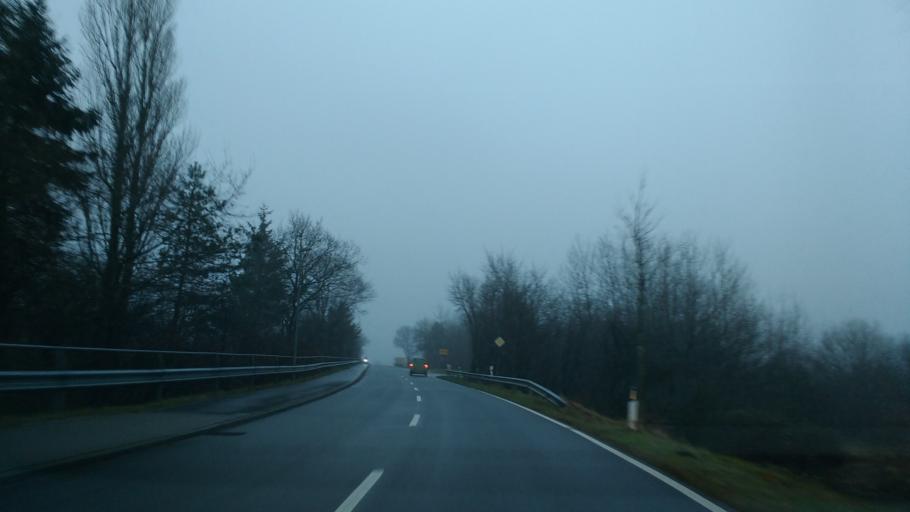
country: DE
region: Schleswig-Holstein
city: Osterronfeld
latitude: 54.2866
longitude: 9.6844
